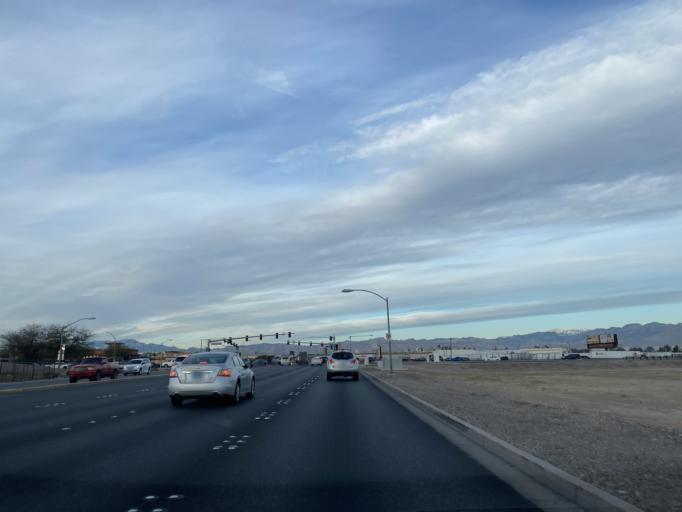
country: US
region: Nevada
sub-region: Clark County
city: Paradise
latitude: 36.0712
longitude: -115.1708
